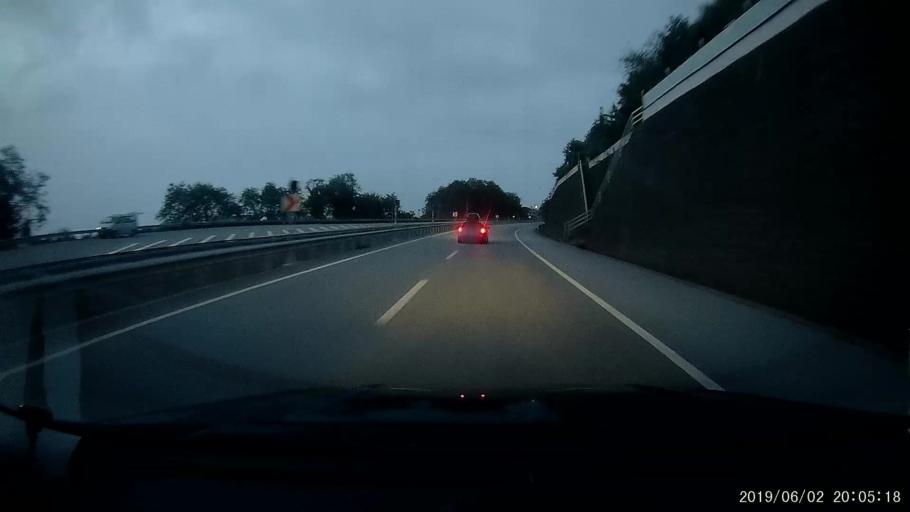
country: TR
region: Giresun
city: Gorele
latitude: 41.0402
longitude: 38.9287
